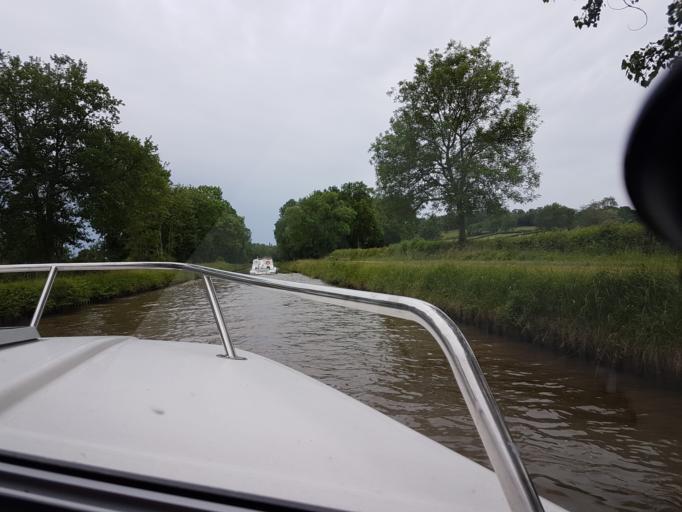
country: FR
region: Bourgogne
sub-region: Departement de la Nievre
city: Clamecy
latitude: 47.3949
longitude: 3.6009
